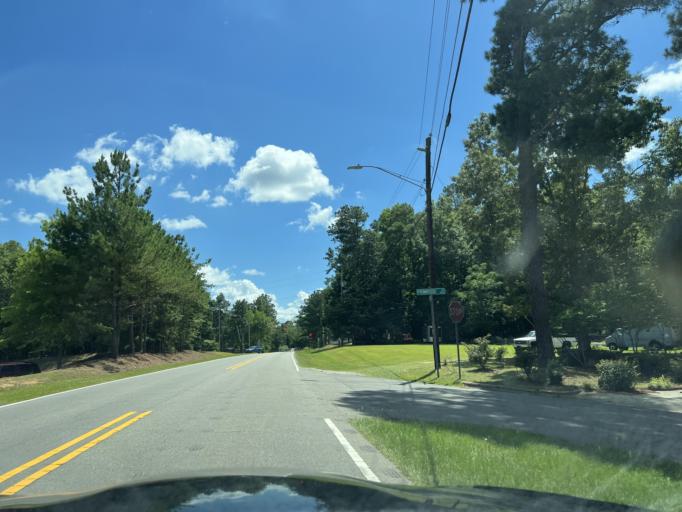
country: US
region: North Carolina
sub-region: Lee County
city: Sanford
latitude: 35.4592
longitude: -79.1652
